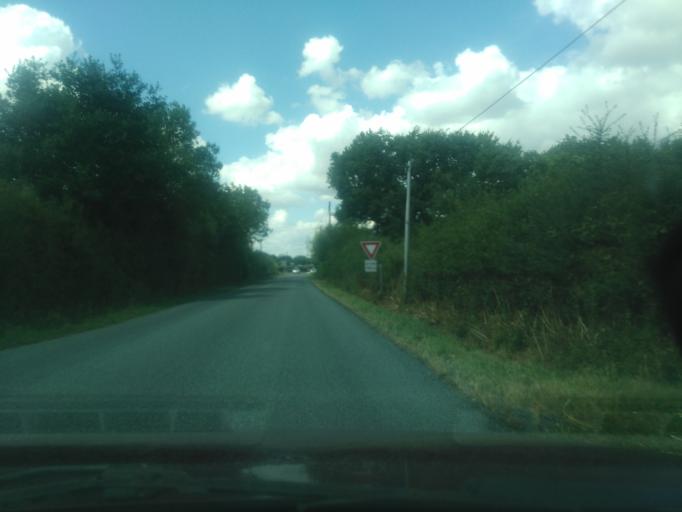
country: FR
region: Pays de la Loire
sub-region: Departement de la Vendee
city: Les Brouzils
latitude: 46.8726
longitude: -1.3199
